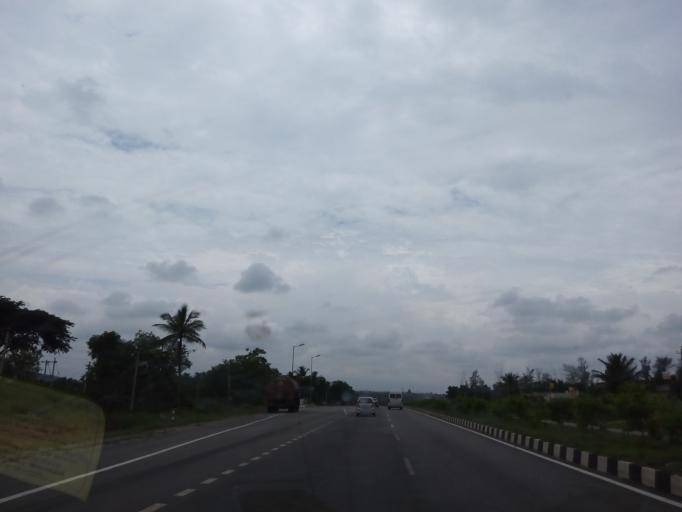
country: IN
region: Karnataka
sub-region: Hassan
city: Channarayapatna
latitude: 12.9763
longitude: 76.3153
